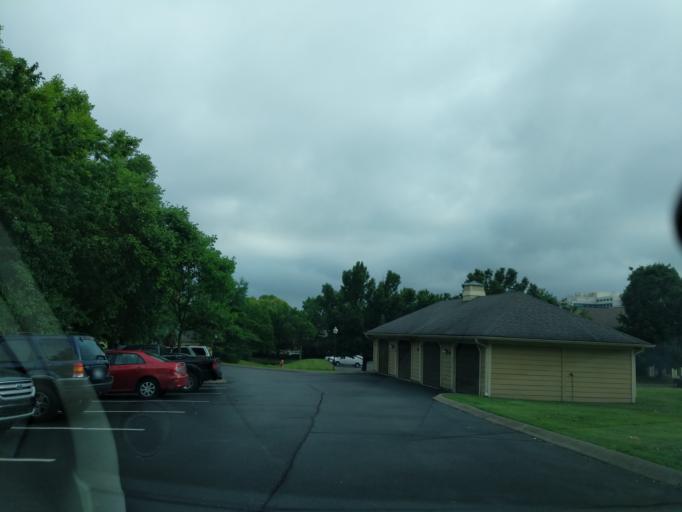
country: US
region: Tennessee
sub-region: Davidson County
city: Lakewood
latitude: 36.1721
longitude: -86.6116
